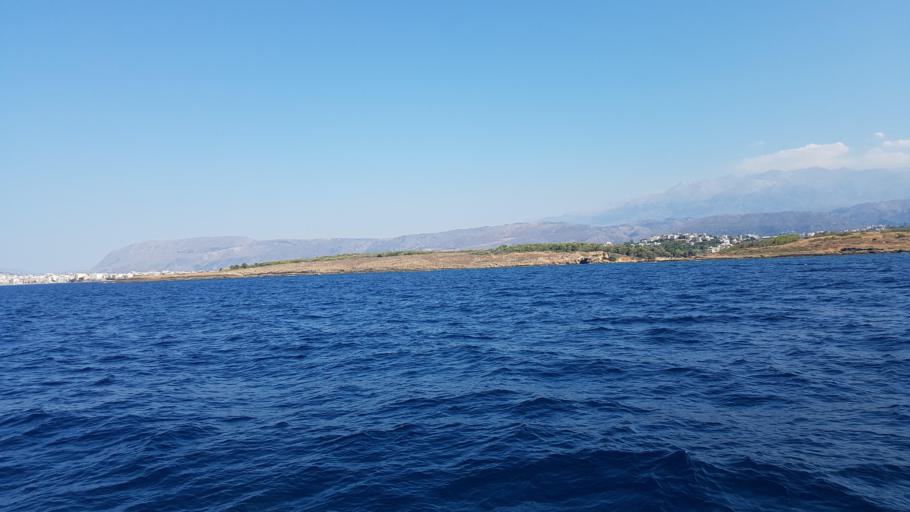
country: GR
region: Crete
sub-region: Nomos Chanias
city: Daratsos
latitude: 35.5219
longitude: 23.9804
